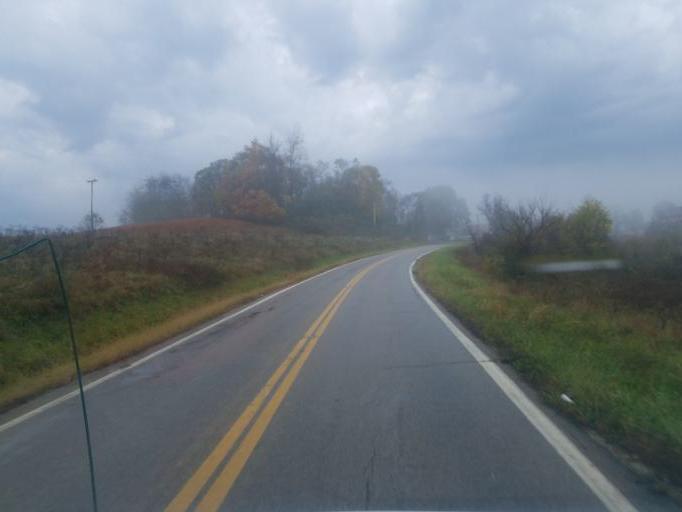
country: US
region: Ohio
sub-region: Morgan County
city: McConnelsville
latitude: 39.4969
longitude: -81.8936
